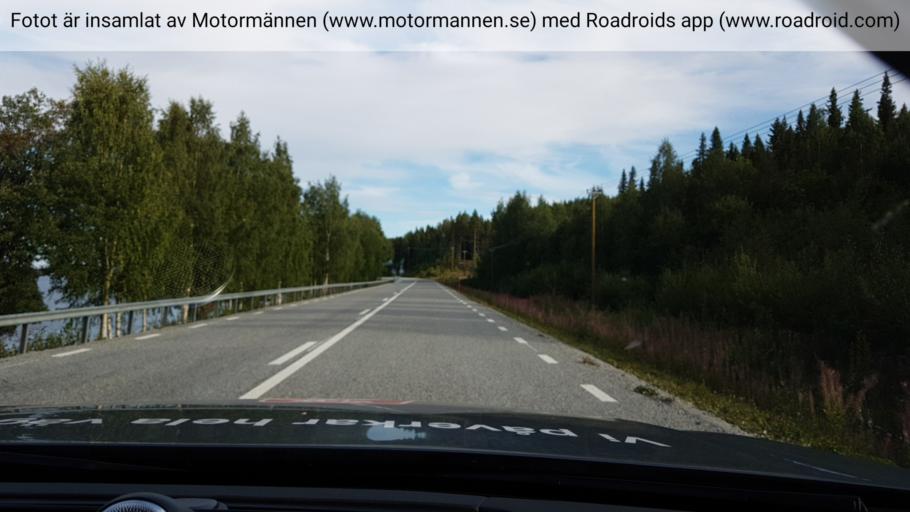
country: SE
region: Jaemtland
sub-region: Stroemsunds Kommun
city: Stroemsund
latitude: 64.1878
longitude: 15.6412
